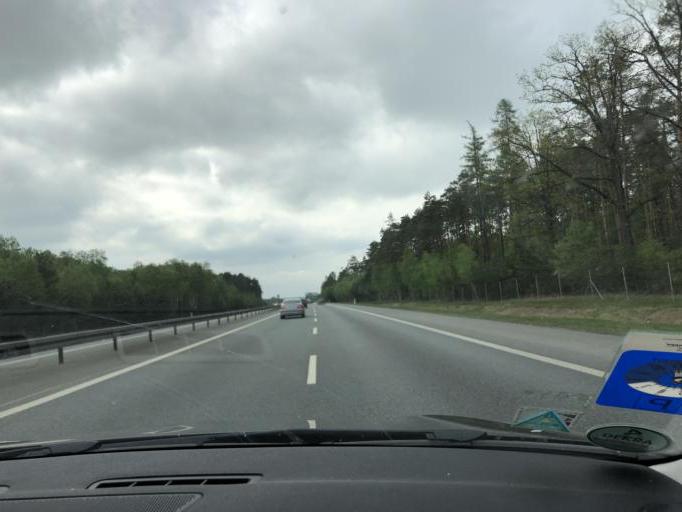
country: PL
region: Opole Voivodeship
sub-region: Powiat opolski
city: Proszkow
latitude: 50.5553
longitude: 17.8843
